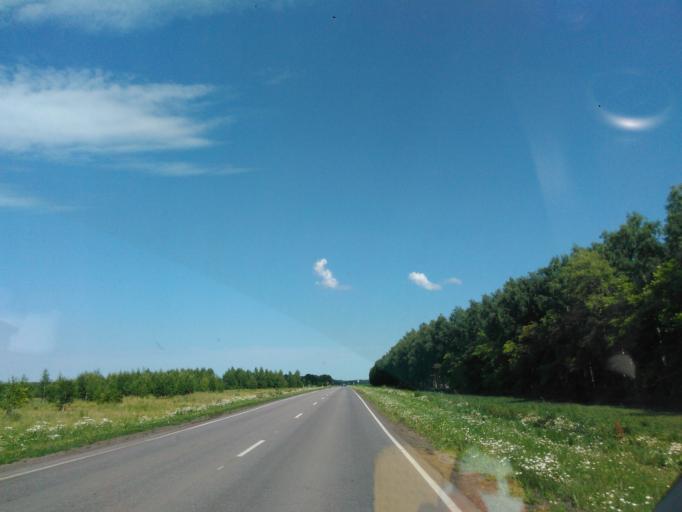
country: RU
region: Penza
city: Belinskiy
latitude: 52.9687
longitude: 43.4733
